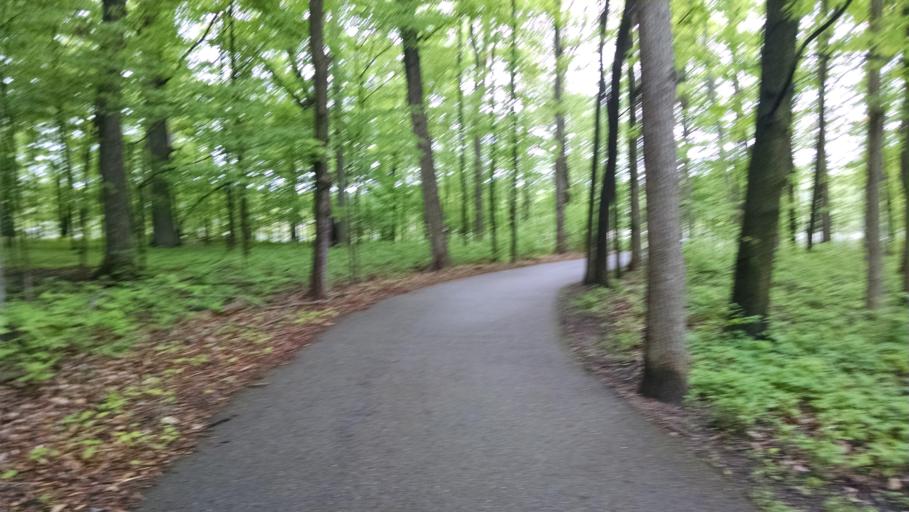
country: US
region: Michigan
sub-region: Eaton County
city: Waverly
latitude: 42.7698
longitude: -84.6343
